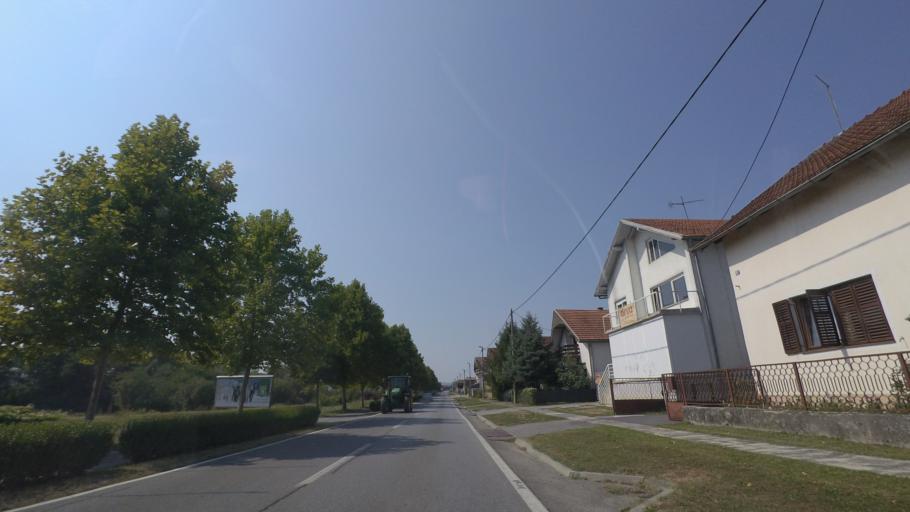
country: HR
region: Pozesko-Slavonska
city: Pakrac
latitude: 45.4223
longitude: 17.1777
